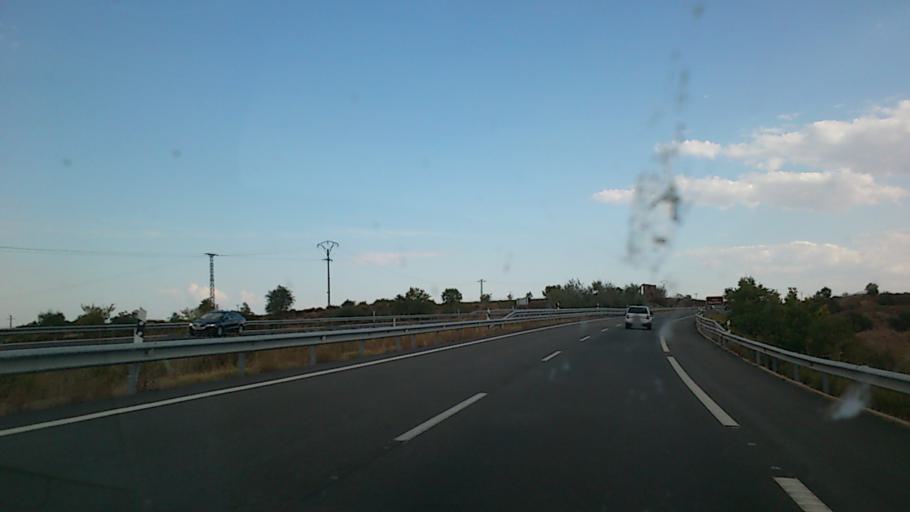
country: ES
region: La Rioja
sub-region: Provincia de La Rioja
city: Aldeanueva de Ebro
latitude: 42.2479
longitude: -1.9057
